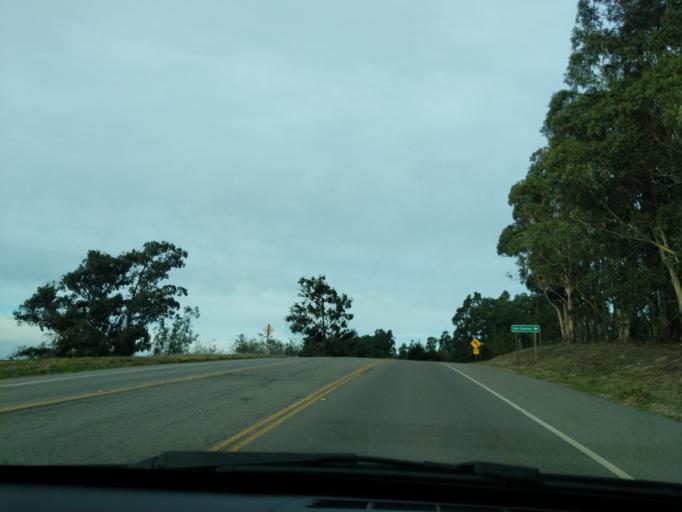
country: US
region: California
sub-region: San Luis Obispo County
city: Callender
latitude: 35.0246
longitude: -120.5619
